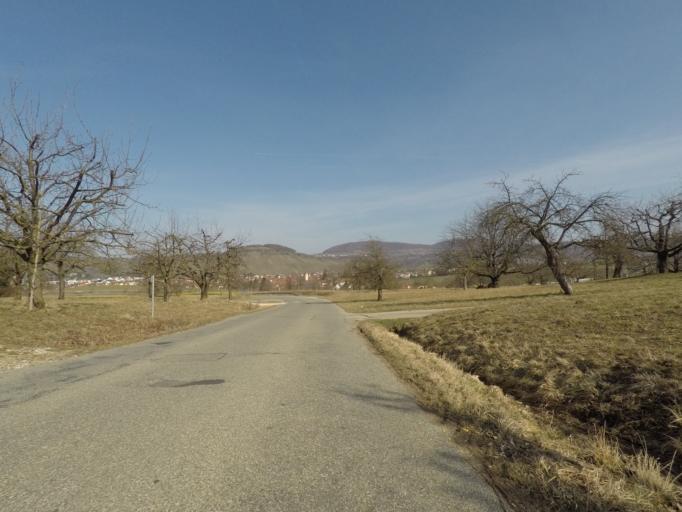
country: DE
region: Baden-Wuerttemberg
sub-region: Tuebingen Region
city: Metzingen
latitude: 48.5235
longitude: 9.3015
